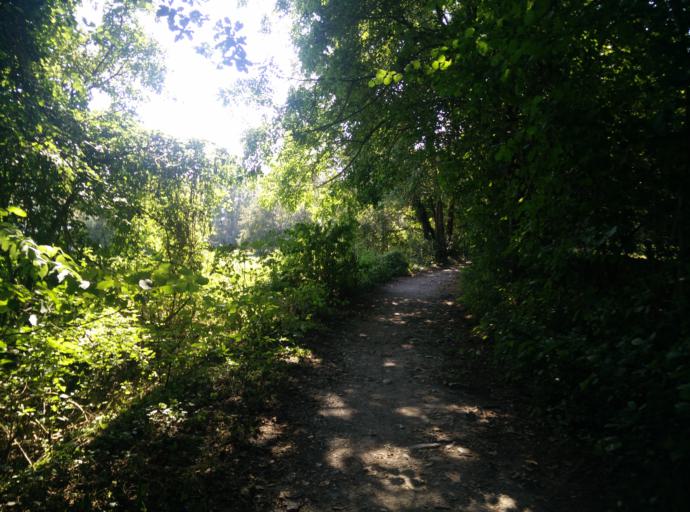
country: IT
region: Piedmont
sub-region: Provincia di Torino
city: Avigliana
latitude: 45.0574
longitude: 7.3842
